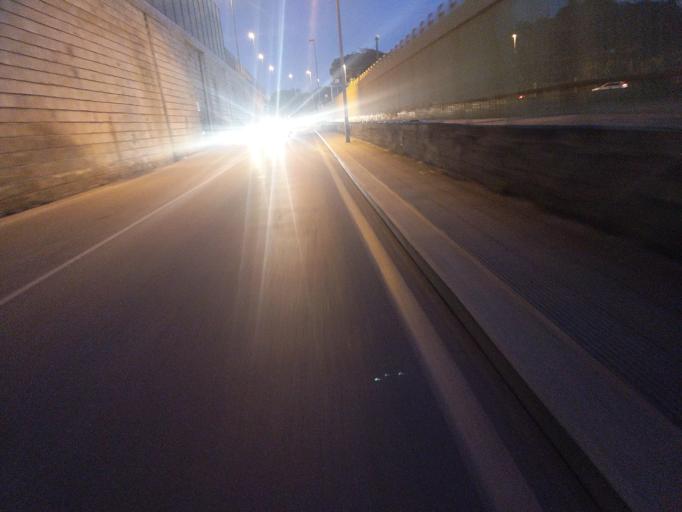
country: IT
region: Apulia
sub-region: Provincia di Bari
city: Modugno
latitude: 41.0891
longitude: 16.7897
